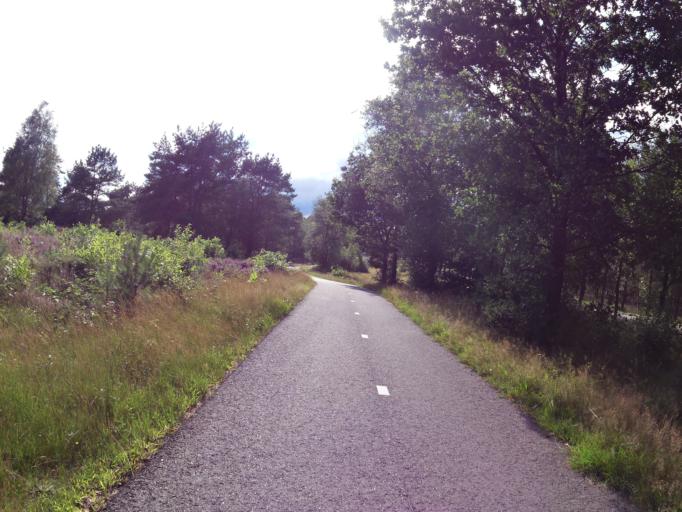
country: NL
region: Gelderland
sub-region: Gemeente Rozendaal
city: Rozendaal
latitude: 52.0381
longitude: 5.9246
